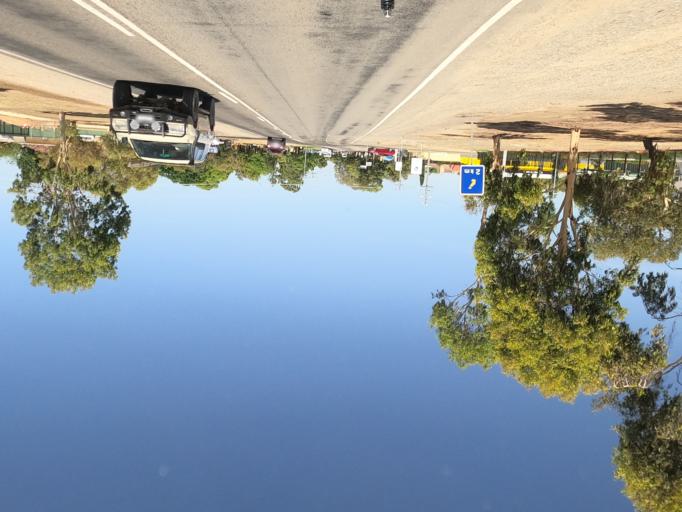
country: AU
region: Victoria
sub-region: Moira
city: Yarrawonga
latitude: -36.0147
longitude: 146.0144
